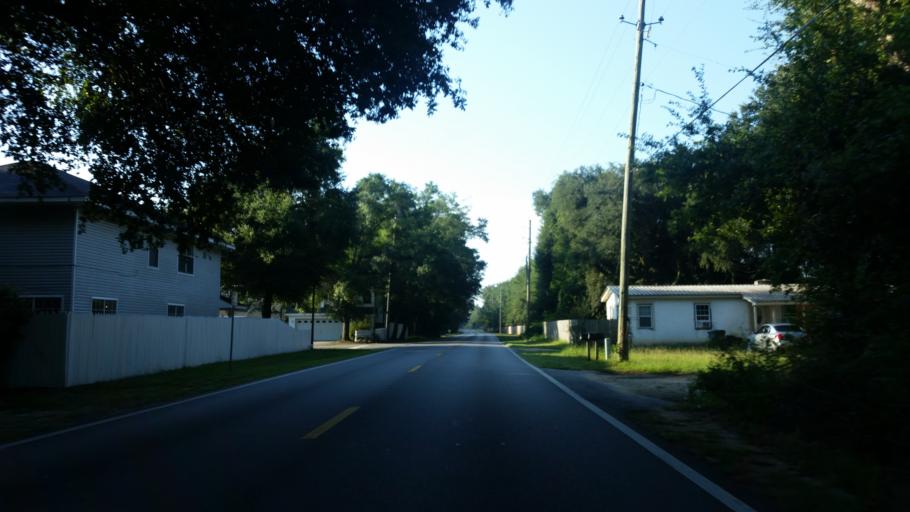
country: US
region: Florida
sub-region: Santa Rosa County
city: Milton
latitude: 30.6241
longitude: -87.0644
